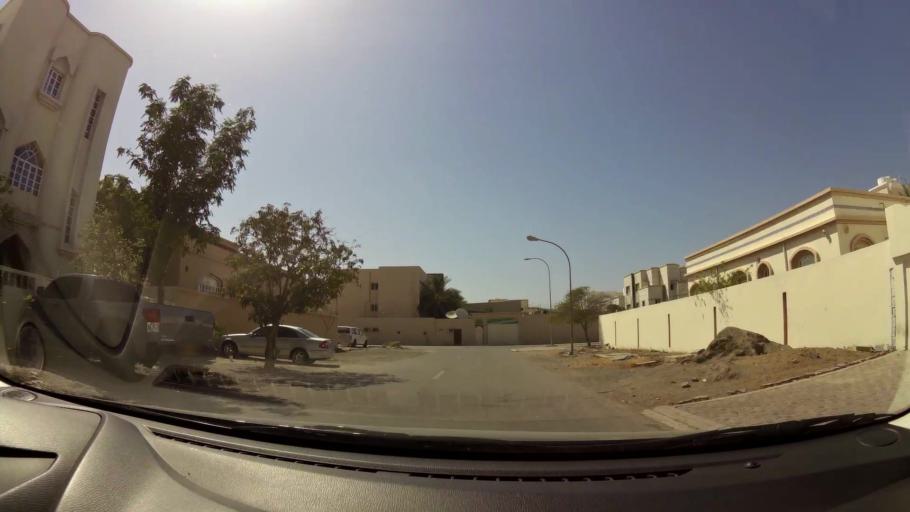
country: OM
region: Muhafazat Masqat
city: As Sib al Jadidah
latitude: 23.6347
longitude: 58.2150
